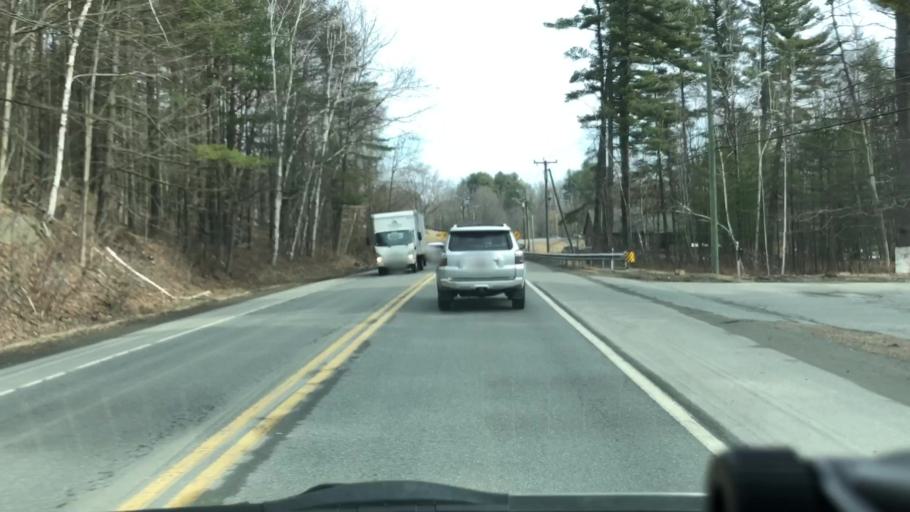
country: US
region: Massachusetts
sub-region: Franklin County
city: Shelburne
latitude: 42.6069
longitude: -72.6724
